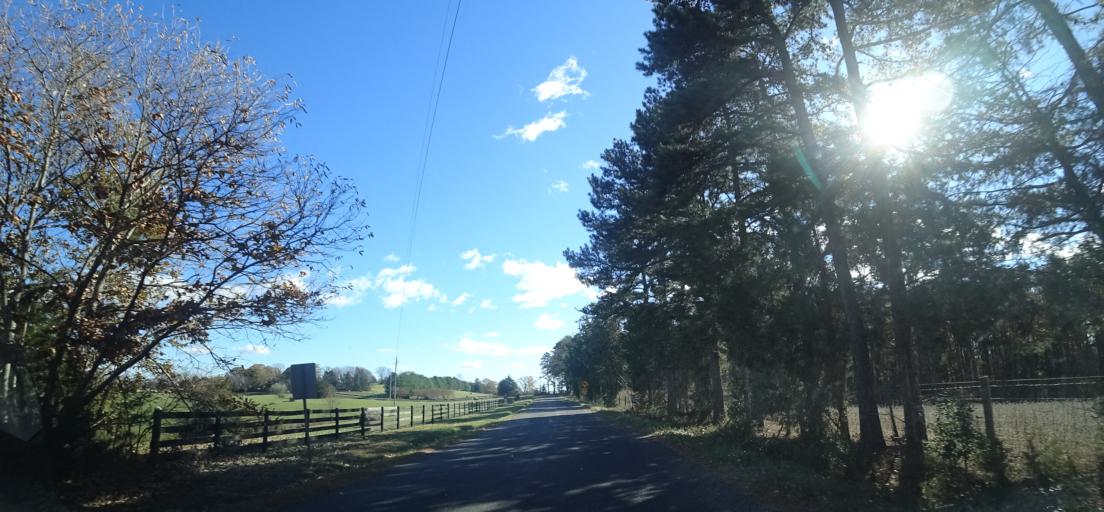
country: US
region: Virginia
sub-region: Greene County
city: Ruckersville
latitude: 38.2596
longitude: -78.3857
